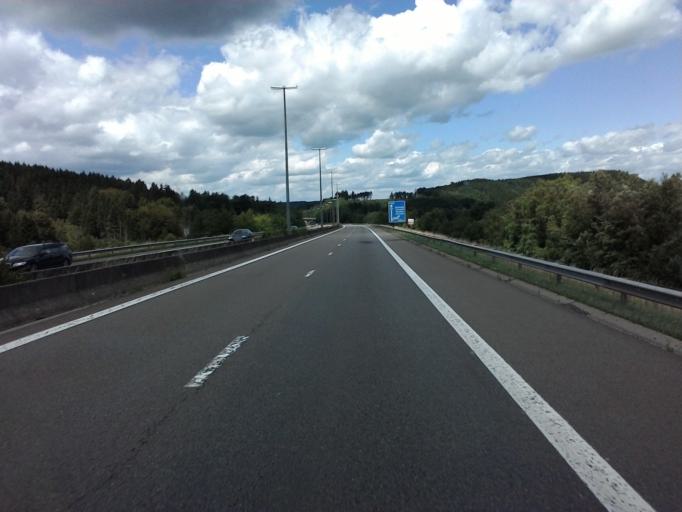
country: BE
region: Wallonia
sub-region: Province du Luxembourg
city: Manhay
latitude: 50.2949
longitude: 5.7252
